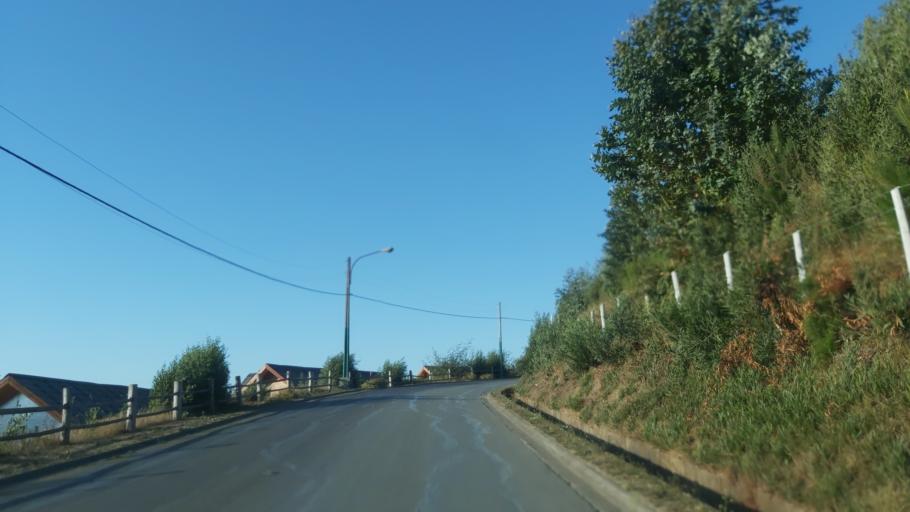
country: CL
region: Biobio
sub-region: Provincia de Concepcion
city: Tome
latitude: -36.5351
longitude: -72.9274
